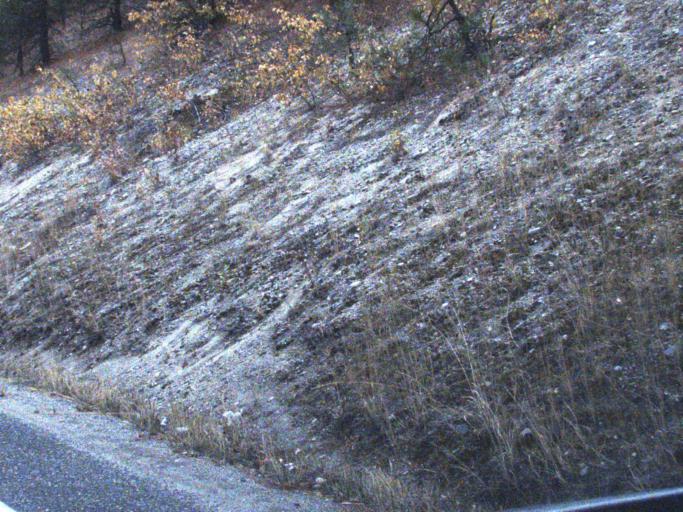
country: US
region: Washington
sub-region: Stevens County
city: Kettle Falls
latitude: 48.6379
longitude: -118.1189
